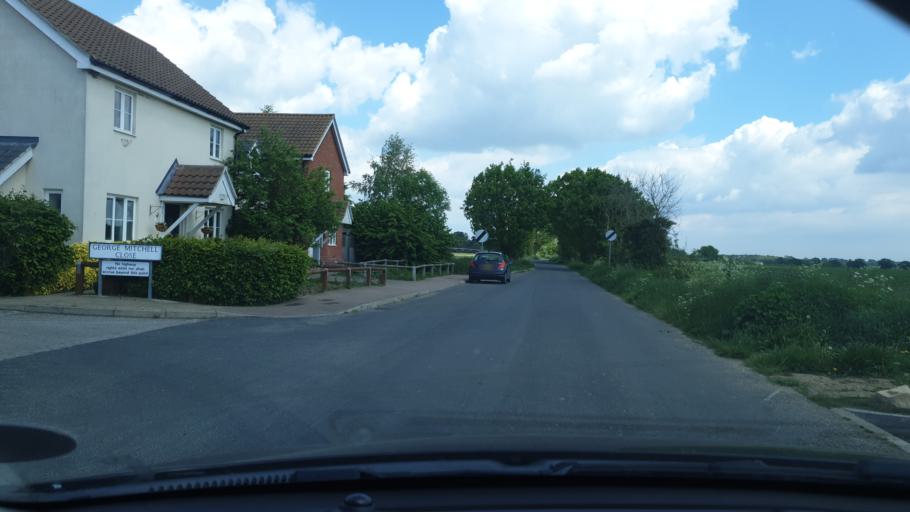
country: GB
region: England
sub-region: Essex
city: Great Bentley
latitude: 51.8431
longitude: 1.0741
